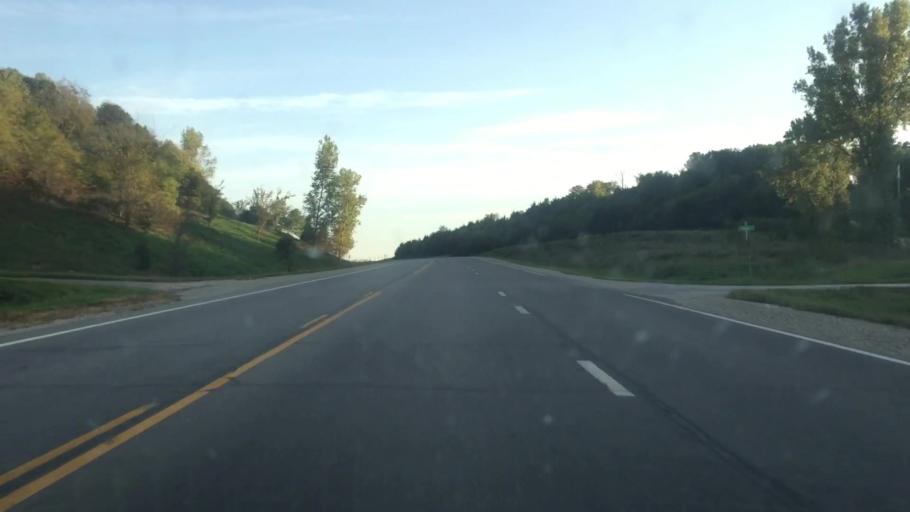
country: US
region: Kansas
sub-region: Atchison County
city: Atchison
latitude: 39.4931
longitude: -95.1317
